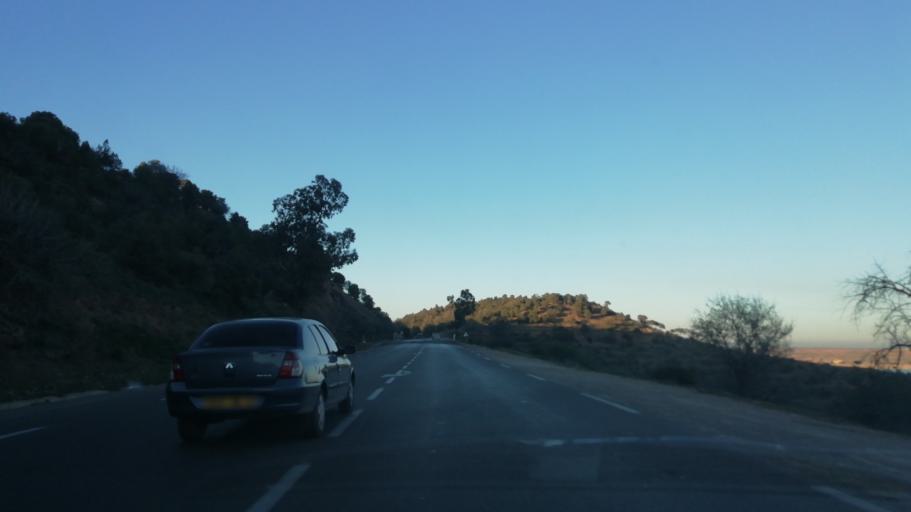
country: DZ
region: Tlemcen
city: Nedroma
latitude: 34.8728
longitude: -1.6688
